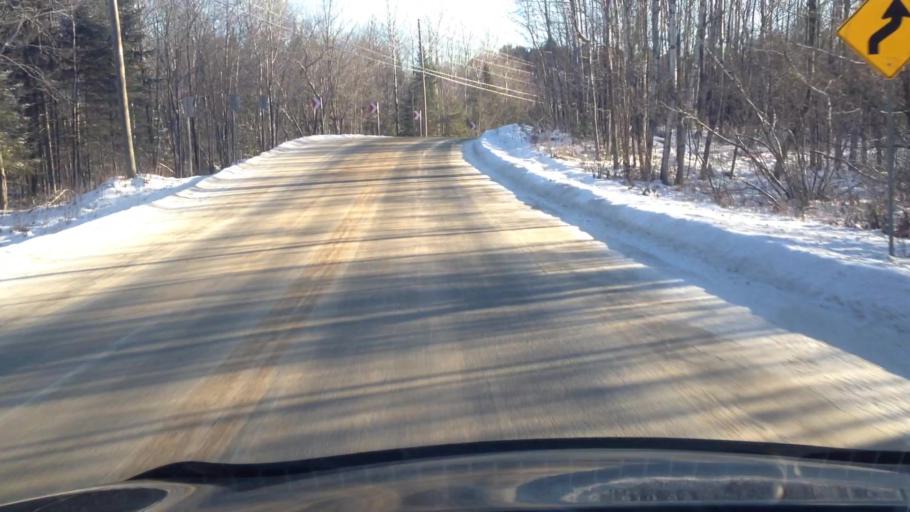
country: CA
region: Quebec
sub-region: Laurentides
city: Brownsburg-Chatham
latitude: 45.9233
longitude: -74.5340
